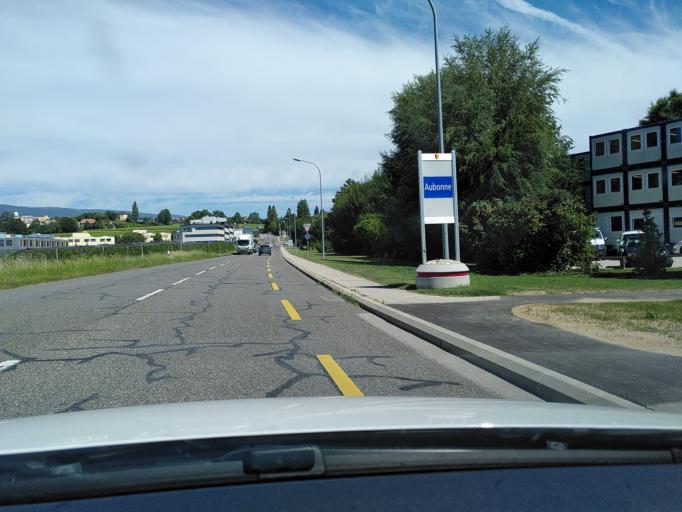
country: CH
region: Vaud
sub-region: Morges District
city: Aubonne
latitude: 46.4866
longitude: 6.3999
